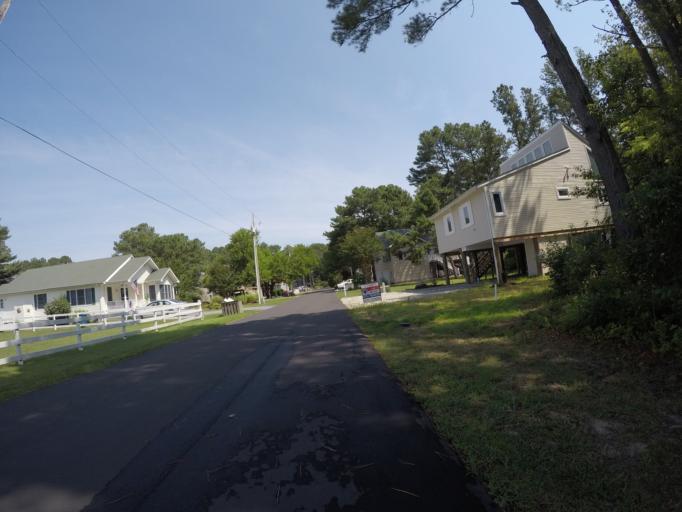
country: US
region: Delaware
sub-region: Sussex County
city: Bethany Beach
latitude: 38.5198
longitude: -75.0599
